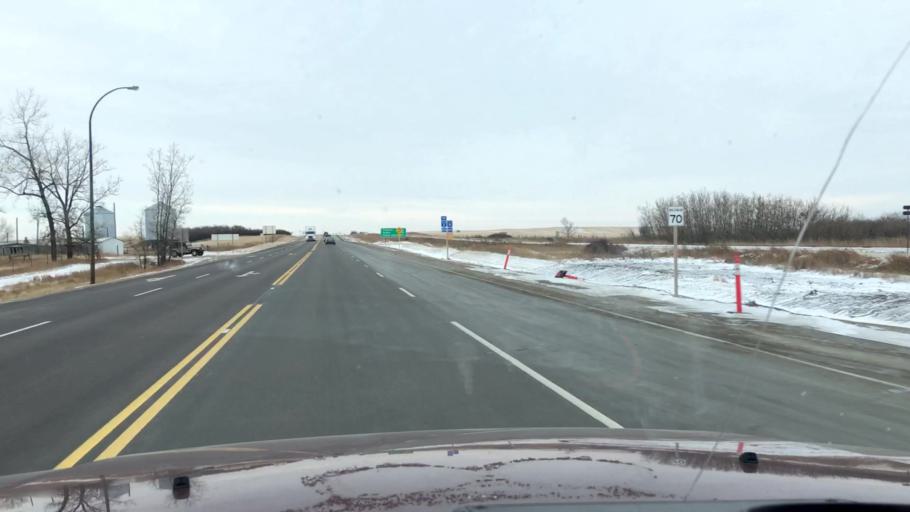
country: CA
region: Saskatchewan
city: Moose Jaw
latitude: 50.8487
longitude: -105.5630
